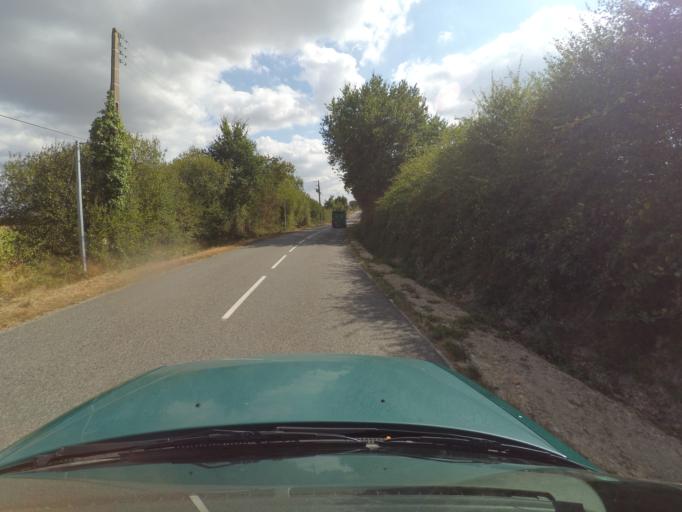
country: FR
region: Pays de la Loire
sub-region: Departement de la Loire-Atlantique
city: La Planche
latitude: 47.0263
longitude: -1.4213
